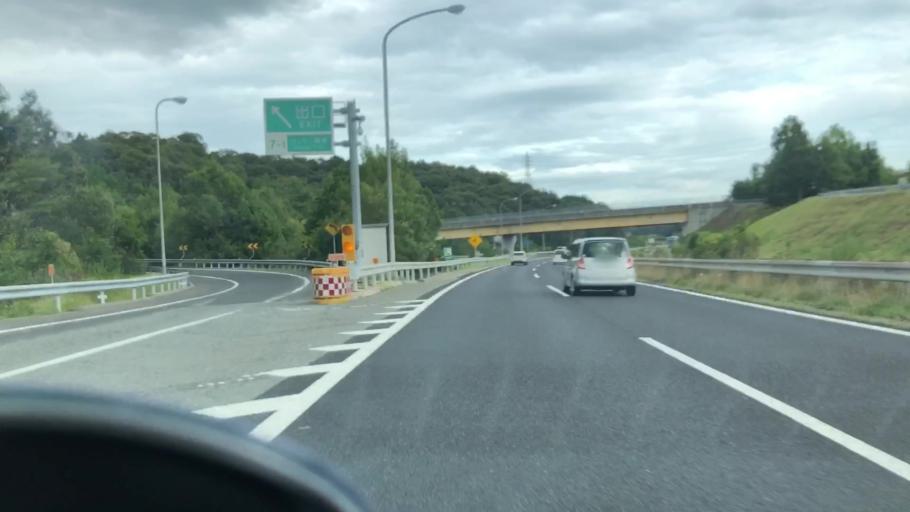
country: JP
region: Hyogo
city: Yashiro
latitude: 34.8967
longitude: 135.0784
